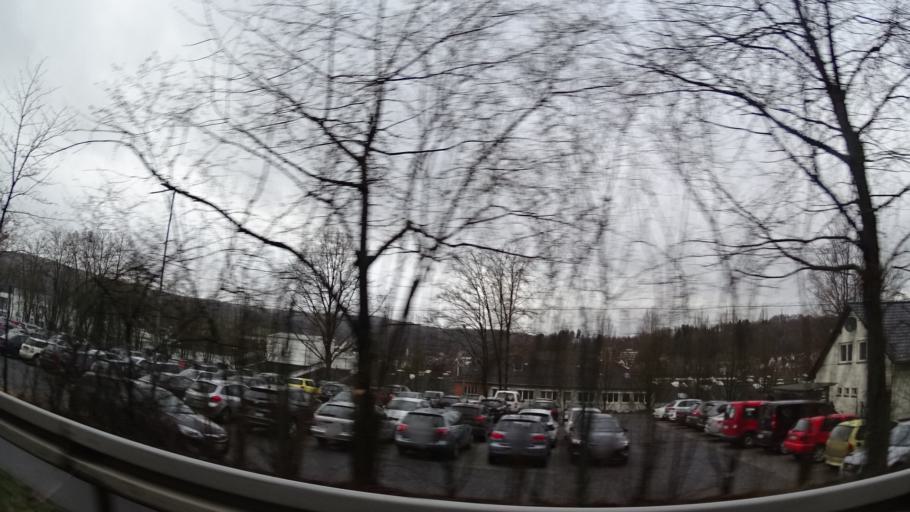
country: DE
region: Hesse
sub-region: Regierungsbezirk Darmstadt
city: Bad Soden-Salmunster
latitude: 50.2857
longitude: 9.3787
